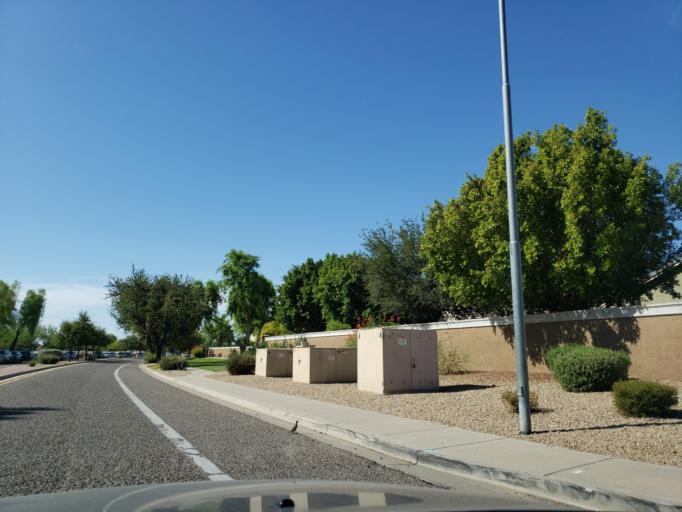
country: US
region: Arizona
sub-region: Maricopa County
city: Peoria
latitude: 33.6646
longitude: -112.1950
